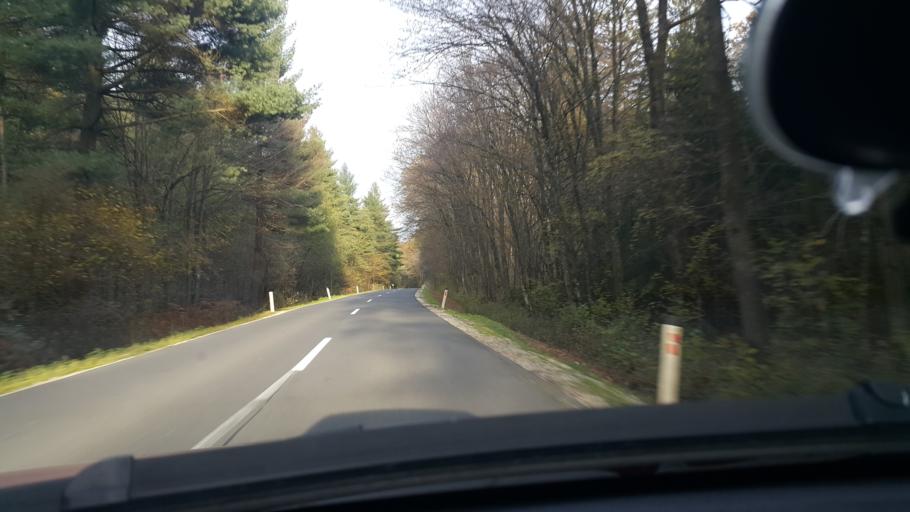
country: SI
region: Brezice
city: Brezice
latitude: 45.9432
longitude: 15.6587
